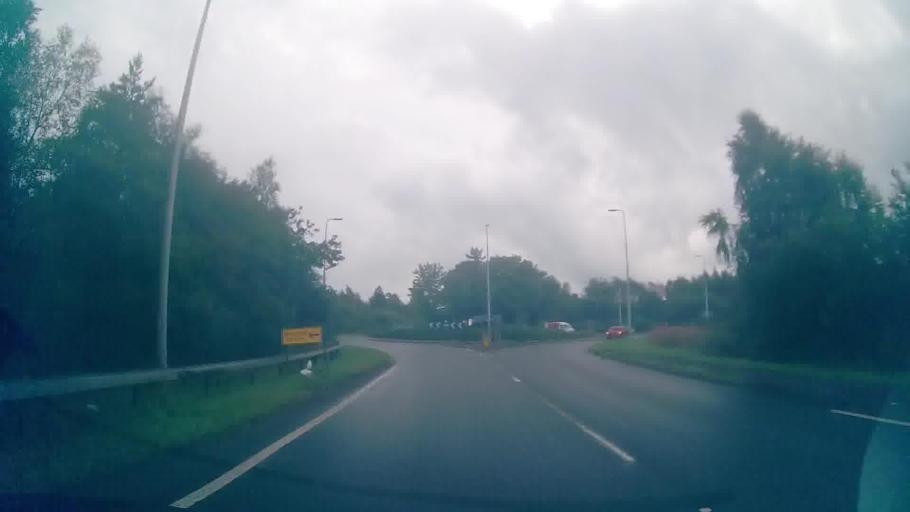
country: GB
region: Scotland
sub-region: Dumfries and Galloway
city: Locharbriggs
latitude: 55.0796
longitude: -3.5719
